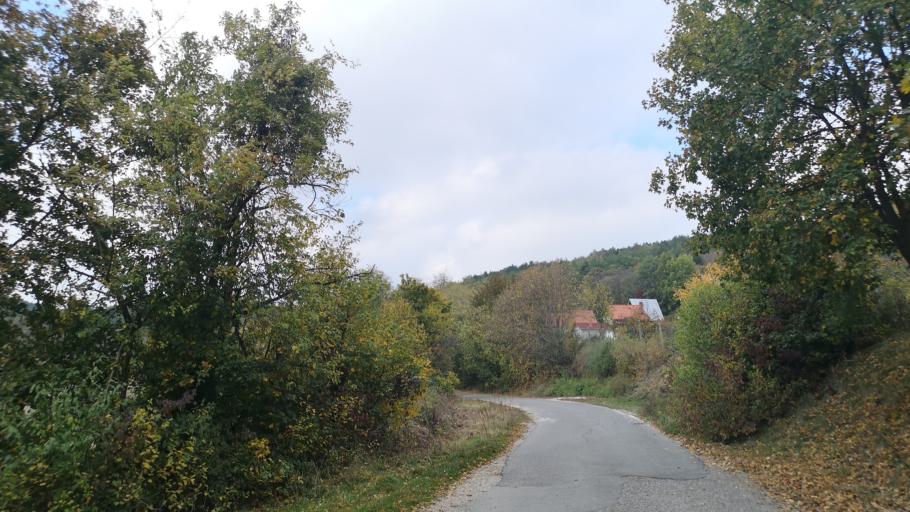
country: SK
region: Nitriansky
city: Cachtice
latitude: 48.7162
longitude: 17.7726
